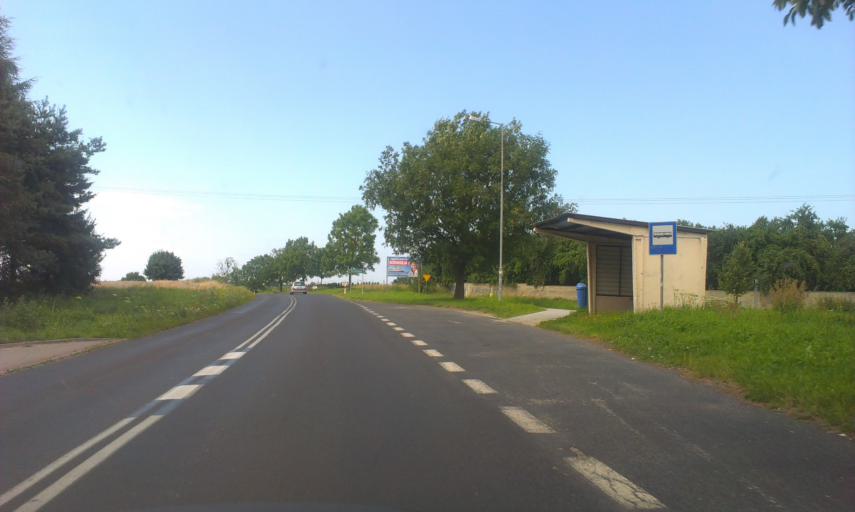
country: PL
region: West Pomeranian Voivodeship
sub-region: Powiat kolobrzeski
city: Kolobrzeg
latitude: 54.1526
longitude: 15.6325
